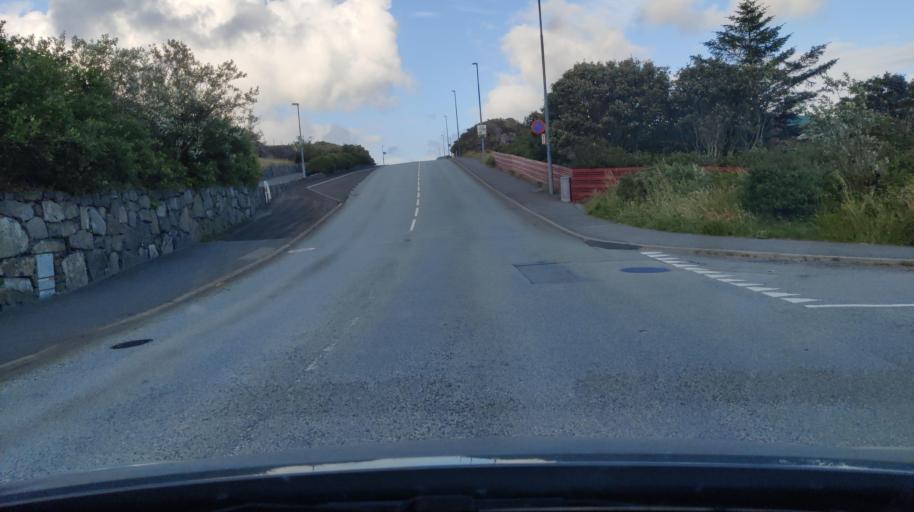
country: FO
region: Streymoy
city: Hoyvik
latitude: 62.0283
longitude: -6.7707
